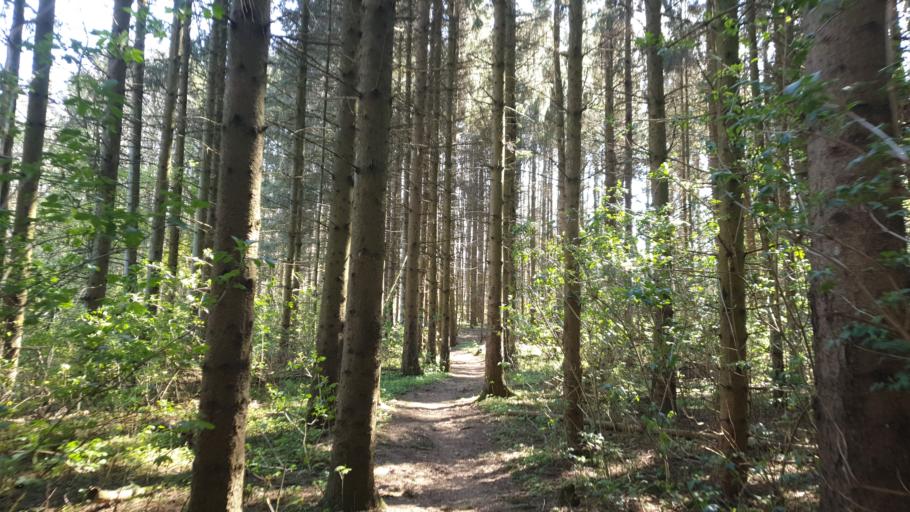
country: DK
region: Central Jutland
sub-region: Hedensted Kommune
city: Hedensted
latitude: 55.8097
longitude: 9.6961
